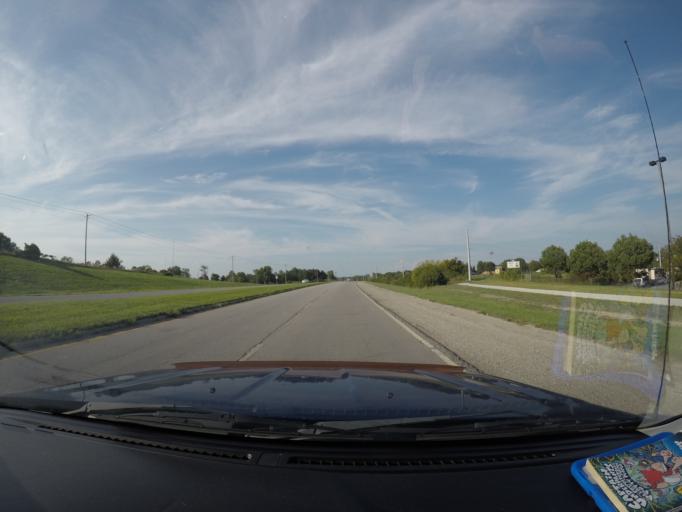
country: US
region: Kansas
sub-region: Atchison County
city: Atchison
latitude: 39.5412
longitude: -95.1314
